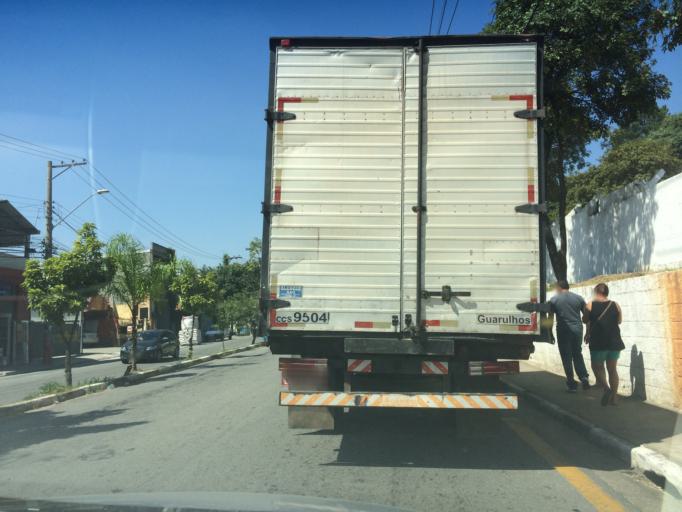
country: BR
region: Sao Paulo
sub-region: Guarulhos
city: Guarulhos
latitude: -23.4337
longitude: -46.5374
